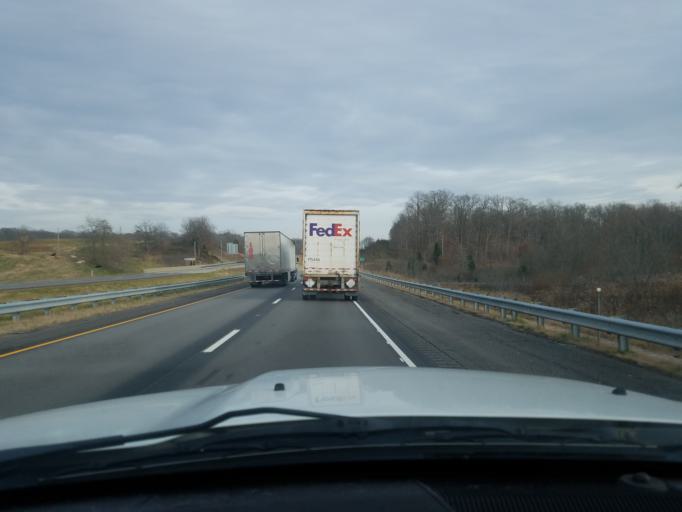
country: US
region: Indiana
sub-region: Dubois County
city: Ferdinand
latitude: 38.2049
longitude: -86.8513
